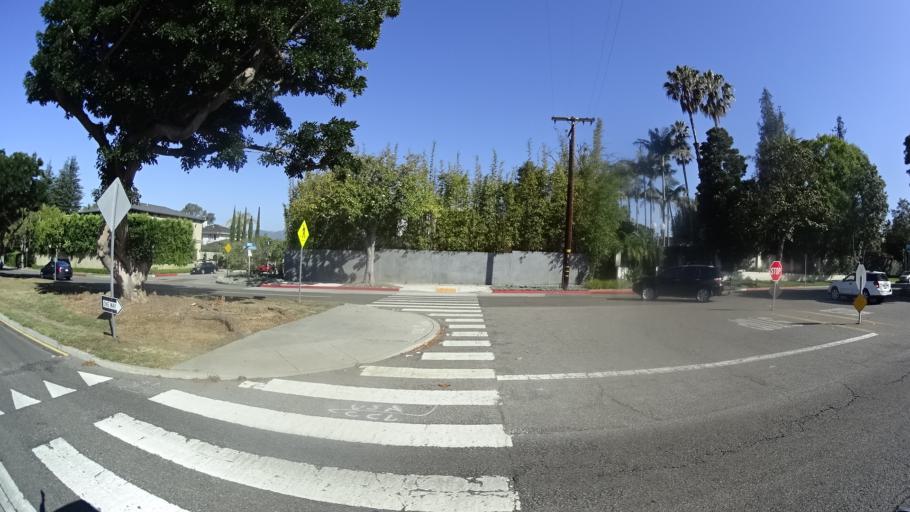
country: US
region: California
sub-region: Los Angeles County
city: Santa Monica
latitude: 34.0418
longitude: -118.5012
